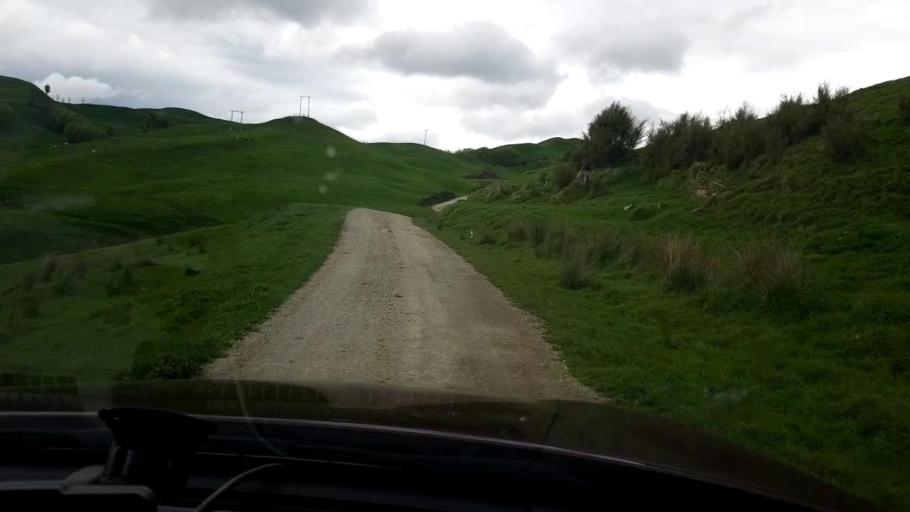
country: NZ
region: Gisborne
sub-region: Gisborne District
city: Gisborne
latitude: -38.3684
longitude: 177.9610
